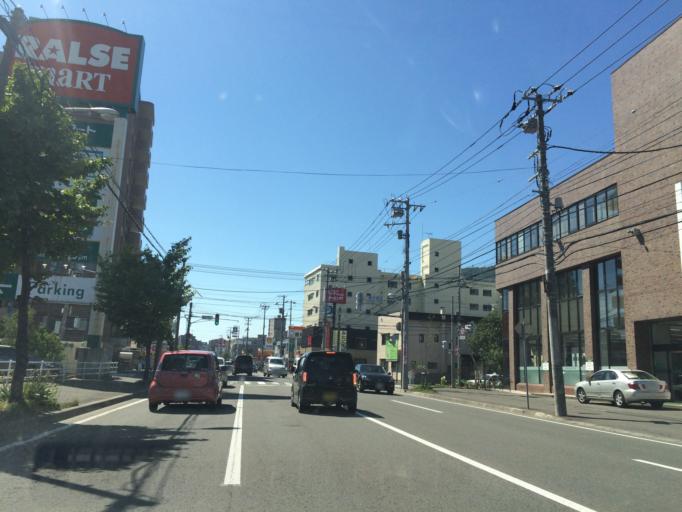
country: JP
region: Hokkaido
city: Sapporo
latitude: 43.0436
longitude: 141.3252
